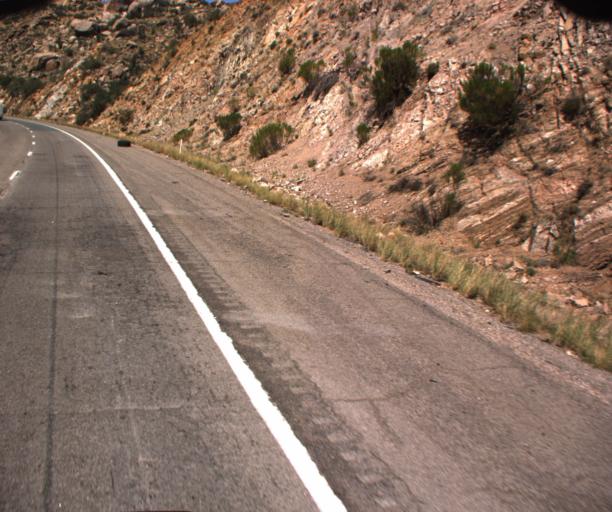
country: US
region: Arizona
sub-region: Mohave County
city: Peach Springs
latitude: 35.1741
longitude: -113.5051
